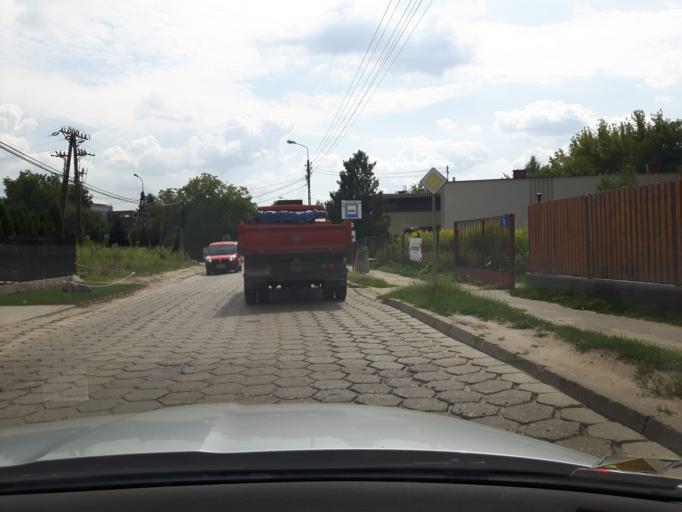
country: PL
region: Masovian Voivodeship
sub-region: Warszawa
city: Wilanow
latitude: 52.2008
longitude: 21.0771
